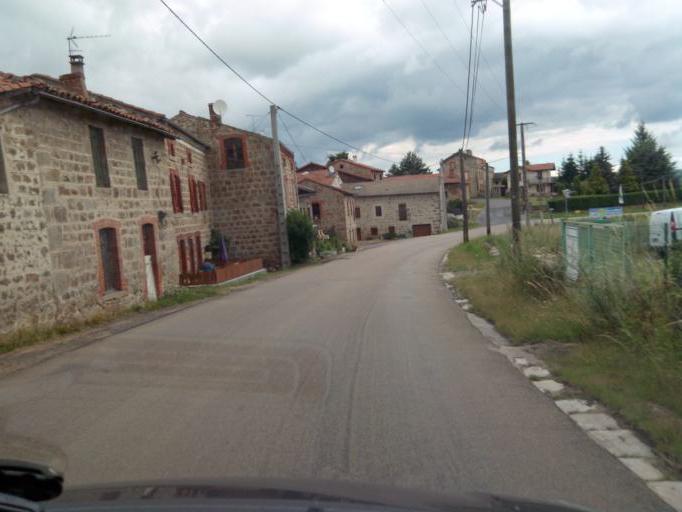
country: FR
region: Rhone-Alpes
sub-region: Departement de la Loire
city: Usson-en-Forez
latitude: 45.3952
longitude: 3.9446
